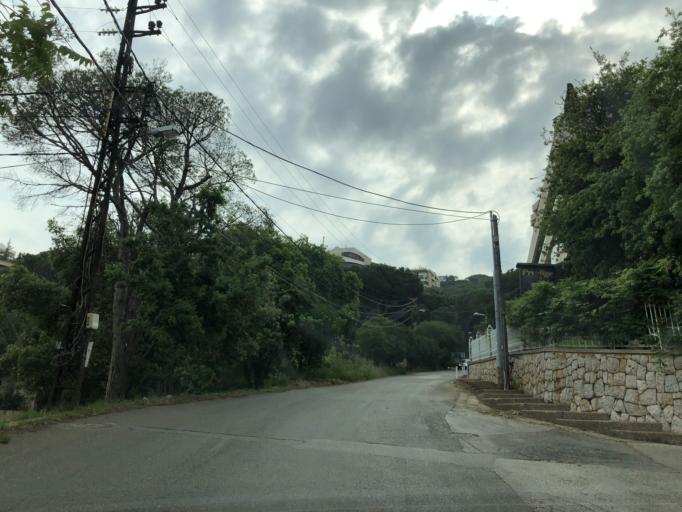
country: LB
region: Mont-Liban
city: Jdaidet el Matn
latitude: 33.8603
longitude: 35.5967
